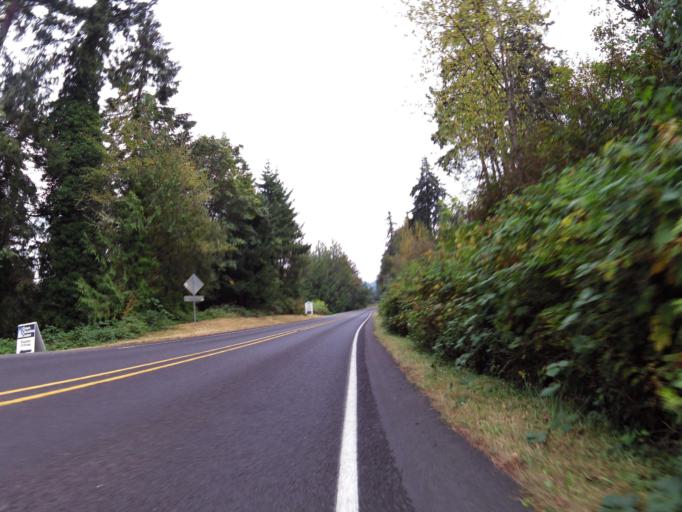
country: US
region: Washington
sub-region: Jefferson County
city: Port Ludlow
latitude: 47.9282
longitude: -122.6846
